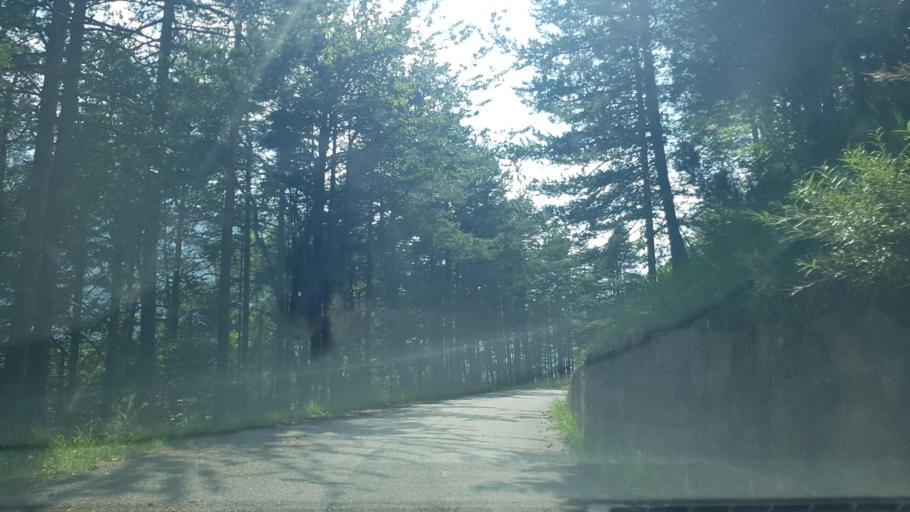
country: IT
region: Friuli Venezia Giulia
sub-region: Provincia di Udine
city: Malborghetto
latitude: 46.4563
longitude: 13.3973
